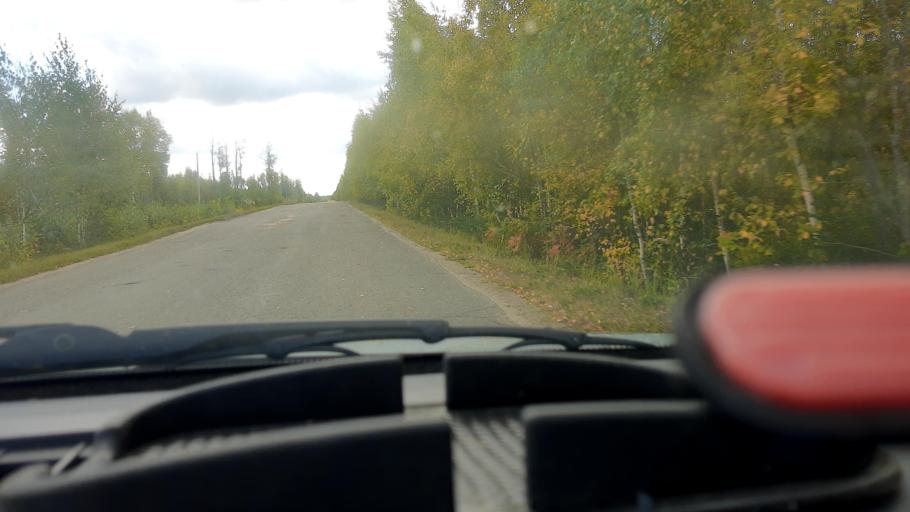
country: RU
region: Mariy-El
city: Kilemary
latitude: 56.8995
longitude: 46.7443
